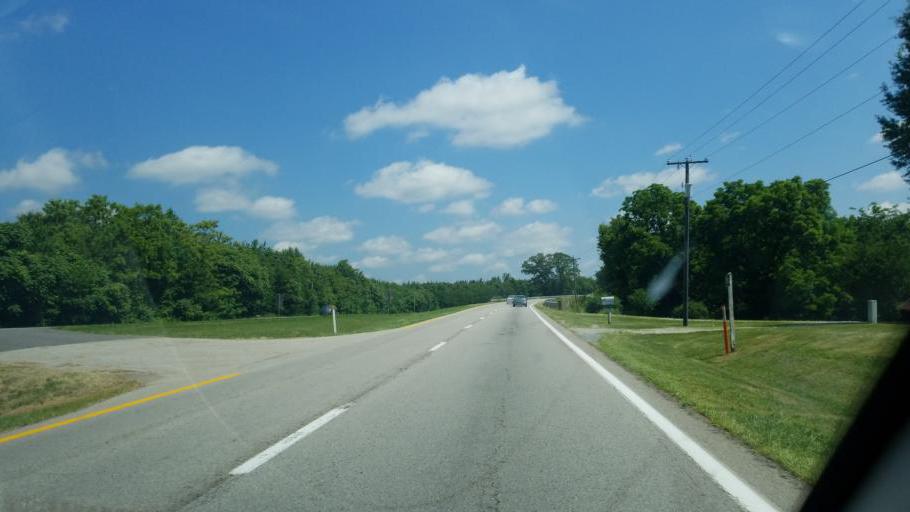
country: US
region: Virginia
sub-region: Pittsylvania County
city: Chatham
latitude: 36.8809
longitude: -79.4083
